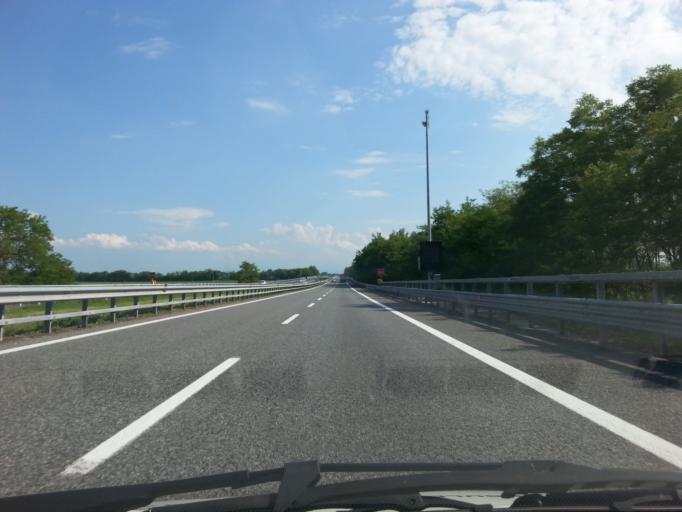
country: IT
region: Piedmont
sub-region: Provincia di Cuneo
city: Caramagna Piemonte
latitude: 44.8051
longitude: 7.7519
